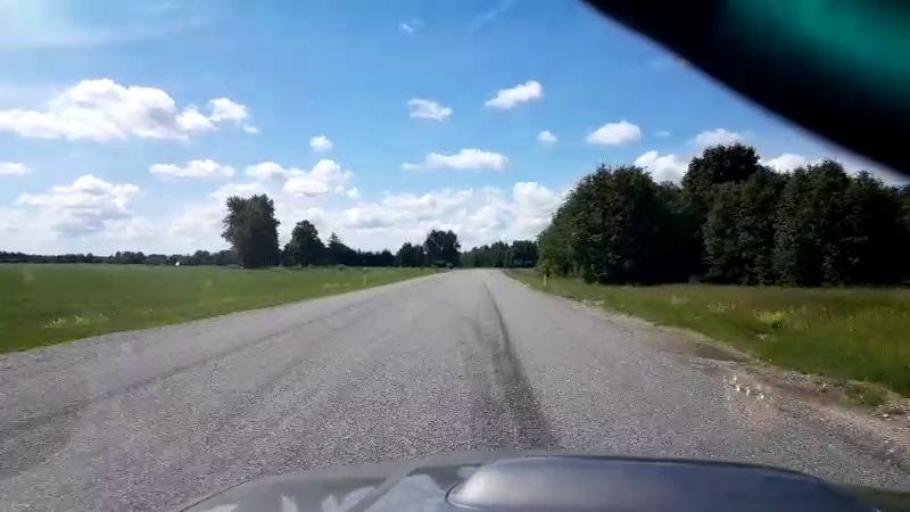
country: EE
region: Laeaene-Virumaa
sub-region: Tapa vald
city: Tapa
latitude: 59.2056
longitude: 25.8499
